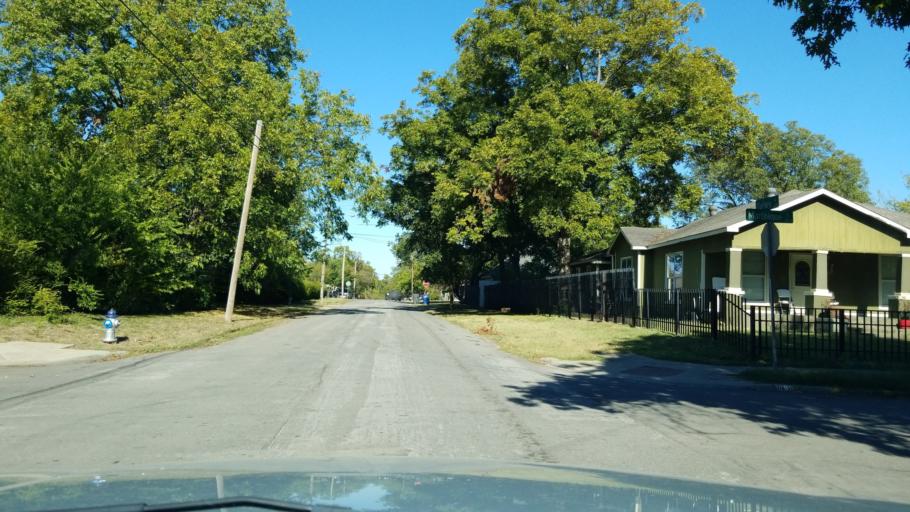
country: US
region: Texas
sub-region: Dallas County
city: Highland Park
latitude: 32.7987
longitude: -96.7453
